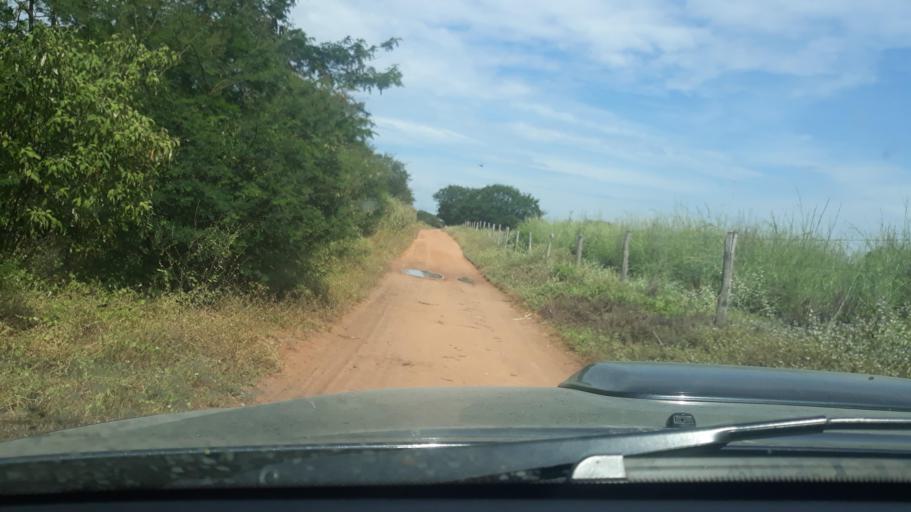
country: BR
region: Bahia
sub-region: Riacho De Santana
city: Riacho de Santana
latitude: -13.8596
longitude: -43.0676
